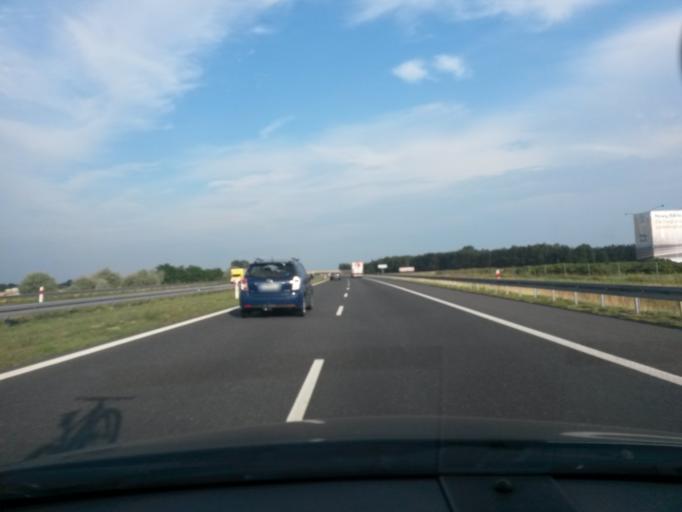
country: PL
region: Lodz Voivodeship
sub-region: Powiat zgierski
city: Parzeczew
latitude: 51.9561
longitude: 19.1355
